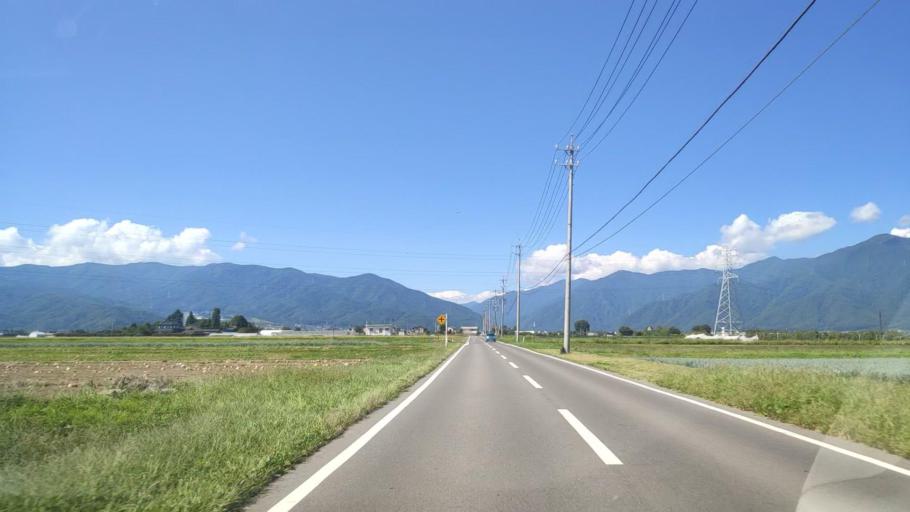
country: JP
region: Nagano
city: Matsumoto
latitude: 36.2007
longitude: 137.8957
